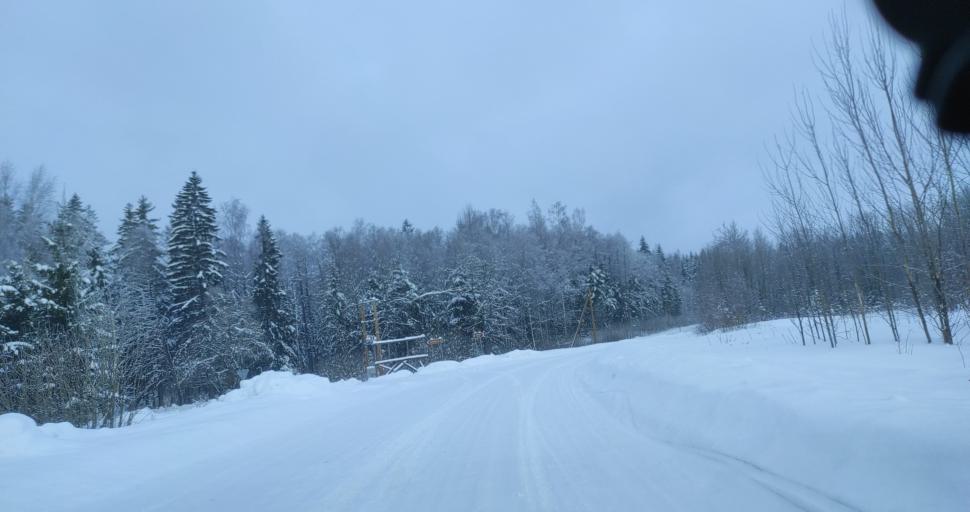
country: LV
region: Vecpiebalga
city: Vecpiebalga
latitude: 56.8709
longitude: 25.9713
